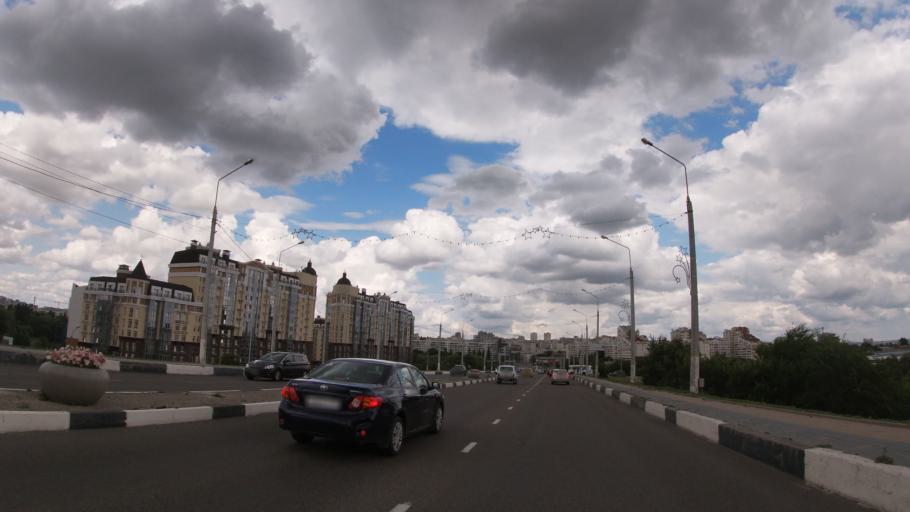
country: RU
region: Belgorod
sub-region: Belgorodskiy Rayon
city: Belgorod
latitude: 50.5871
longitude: 36.5880
